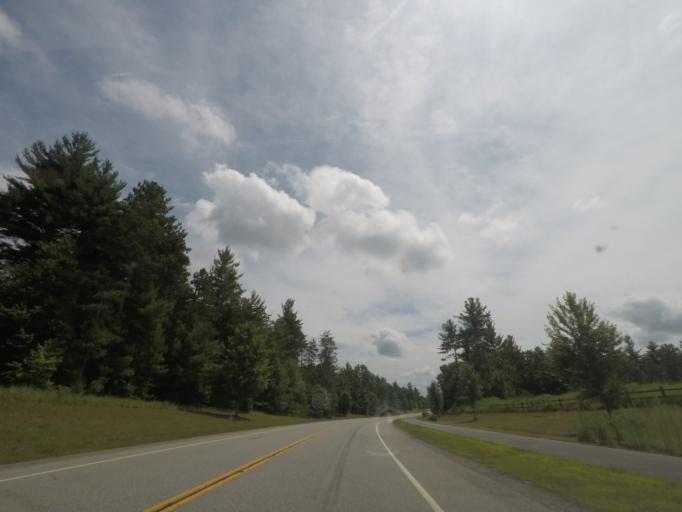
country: US
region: New York
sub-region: Saratoga County
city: Country Knolls
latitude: 42.9595
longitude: -73.7605
